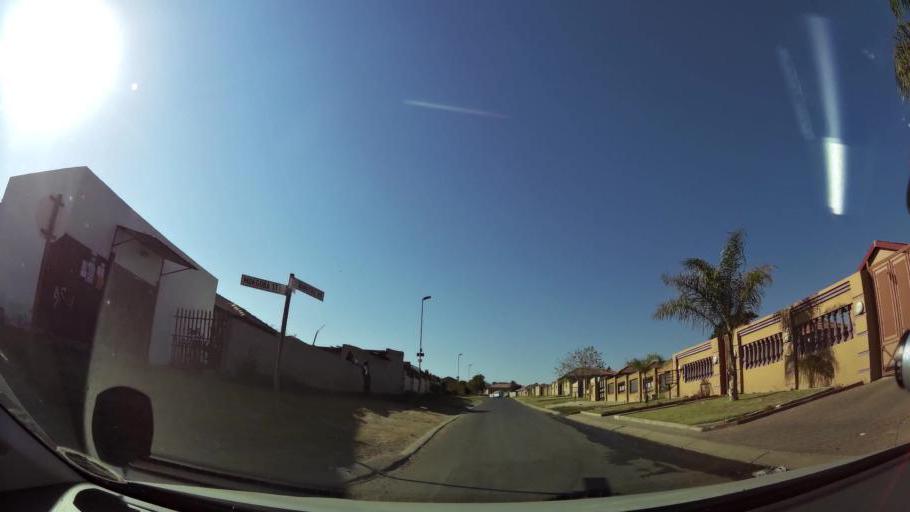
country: ZA
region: Gauteng
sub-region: City of Johannesburg Metropolitan Municipality
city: Modderfontein
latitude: -26.0476
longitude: 28.1994
